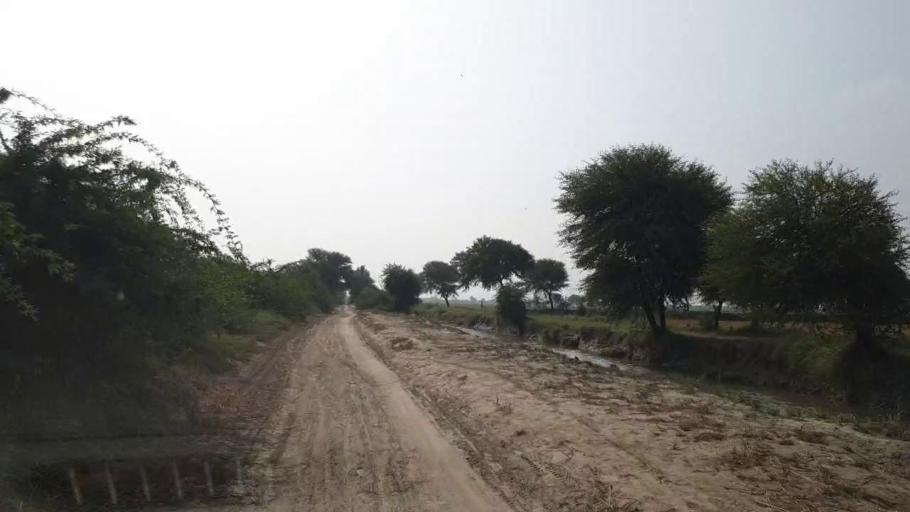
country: PK
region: Sindh
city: Kario
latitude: 24.7671
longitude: 68.5637
